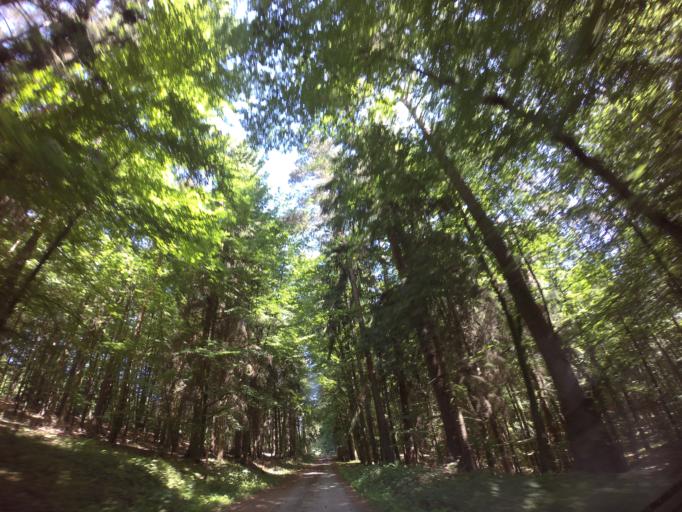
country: PL
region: West Pomeranian Voivodeship
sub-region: Powiat choszczenski
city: Recz
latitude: 53.3142
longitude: 15.6031
